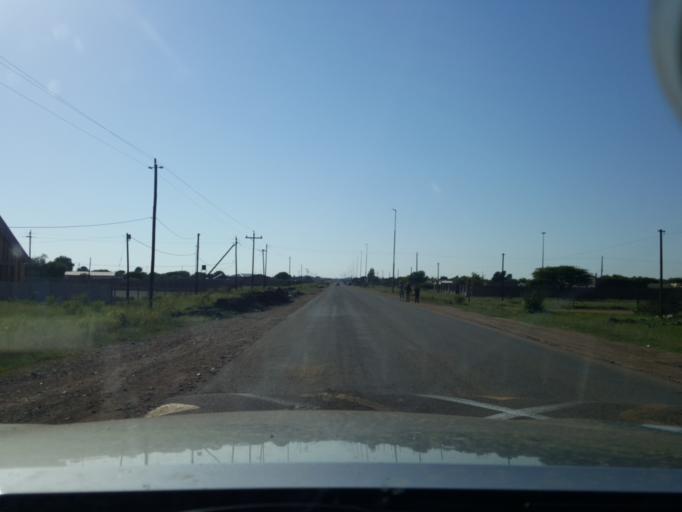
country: ZA
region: North-West
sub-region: Ngaka Modiri Molema District Municipality
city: Mmabatho
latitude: -25.8324
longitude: 25.6585
